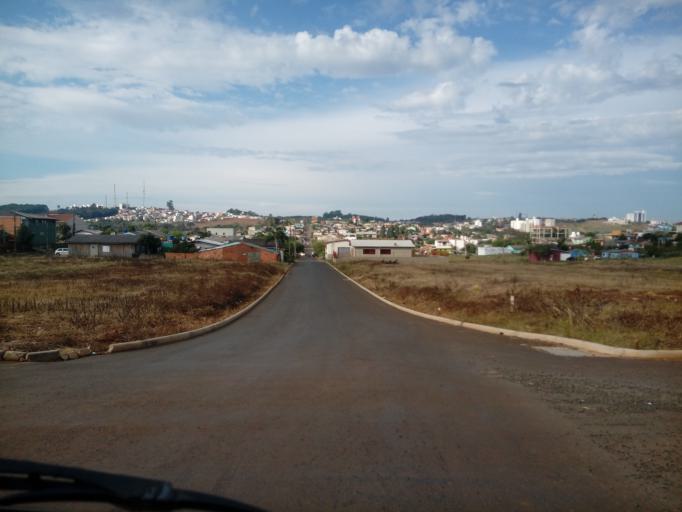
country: BR
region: Santa Catarina
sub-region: Chapeco
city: Chapeco
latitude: -27.0912
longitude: -52.5923
